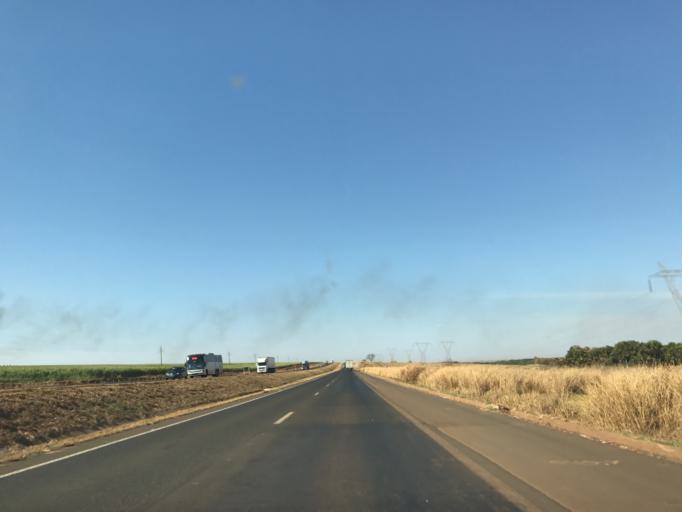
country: BR
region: Goias
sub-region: Goiatuba
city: Goiatuba
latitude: -17.9201
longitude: -49.2414
